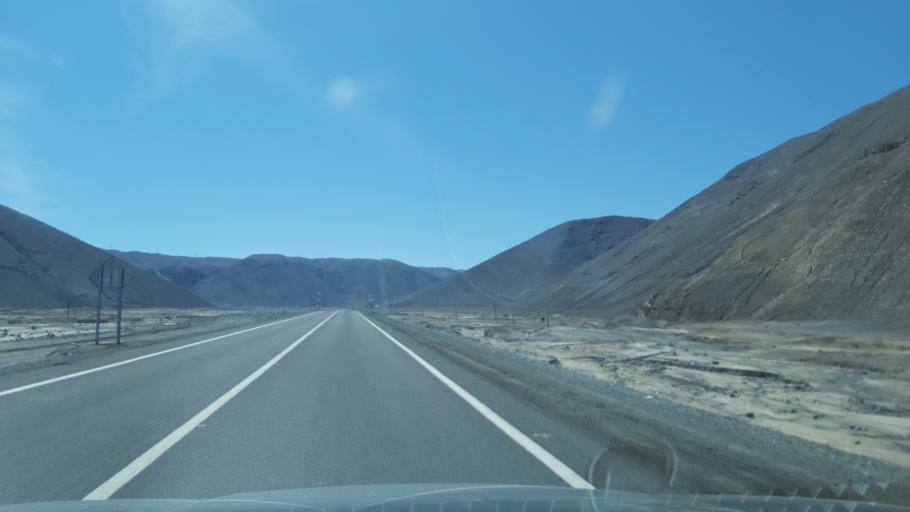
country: CL
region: Atacama
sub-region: Provincia de Chanaral
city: Diego de Almagro
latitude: -26.3319
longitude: -69.8125
